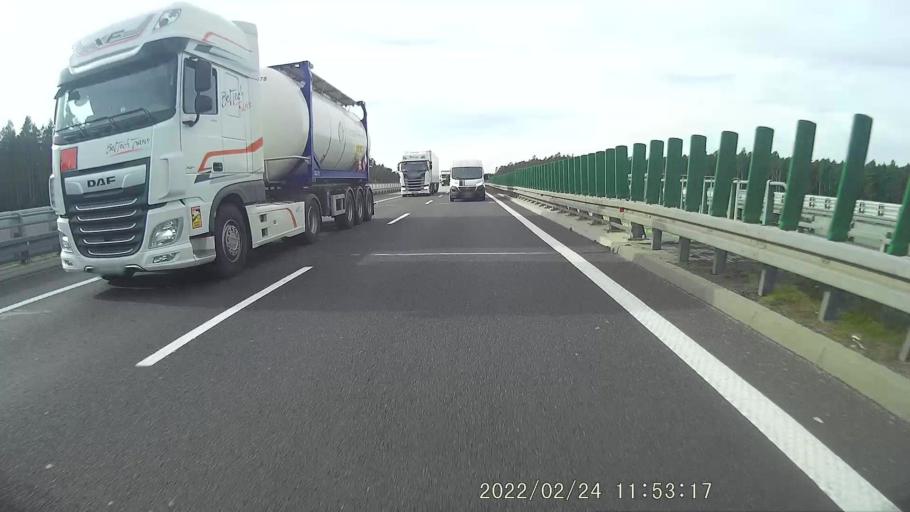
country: PL
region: Lower Silesian Voivodeship
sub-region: Powiat polkowicki
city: Radwanice
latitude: 51.6284
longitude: 15.9764
